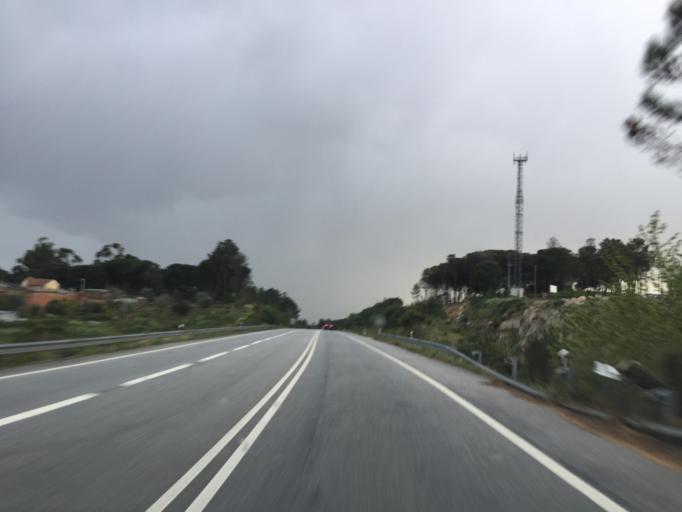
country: PT
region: Viseu
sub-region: Viseu
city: Viseu
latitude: 40.6110
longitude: -7.9603
